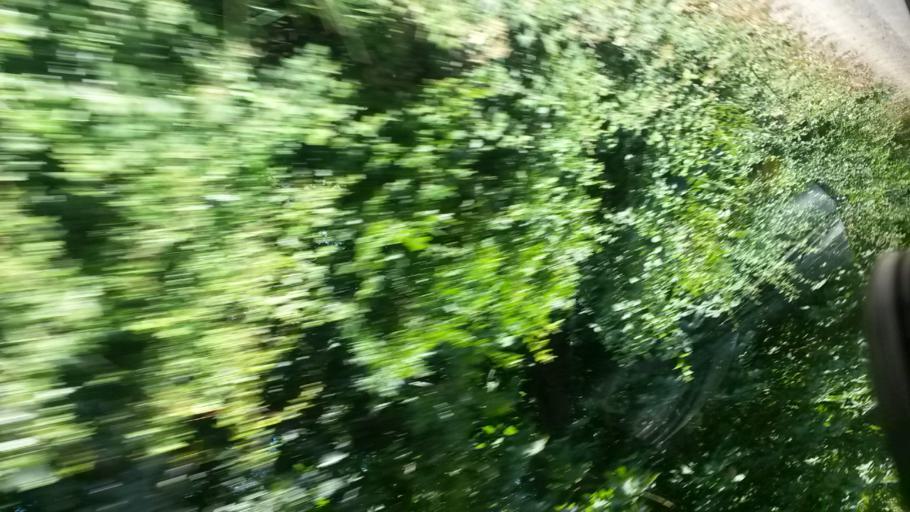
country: IE
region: Leinster
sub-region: Fingal County
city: Swords
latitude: 53.5149
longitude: -6.2408
